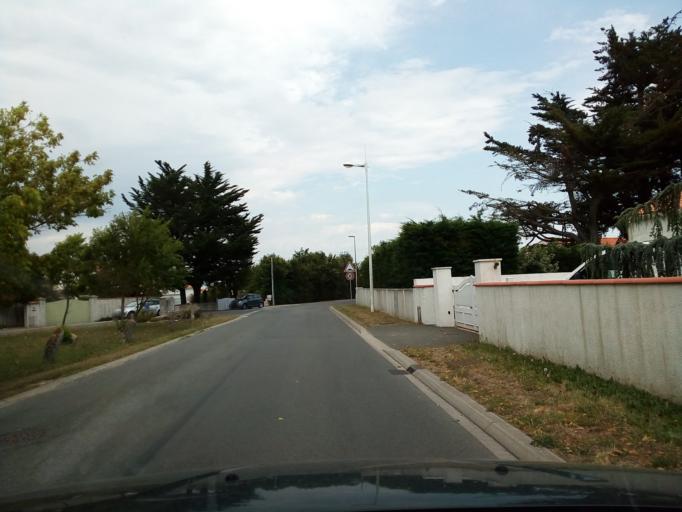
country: FR
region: Poitou-Charentes
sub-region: Departement de la Charente-Maritime
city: Dolus-d'Oleron
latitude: 45.9455
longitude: -1.3002
